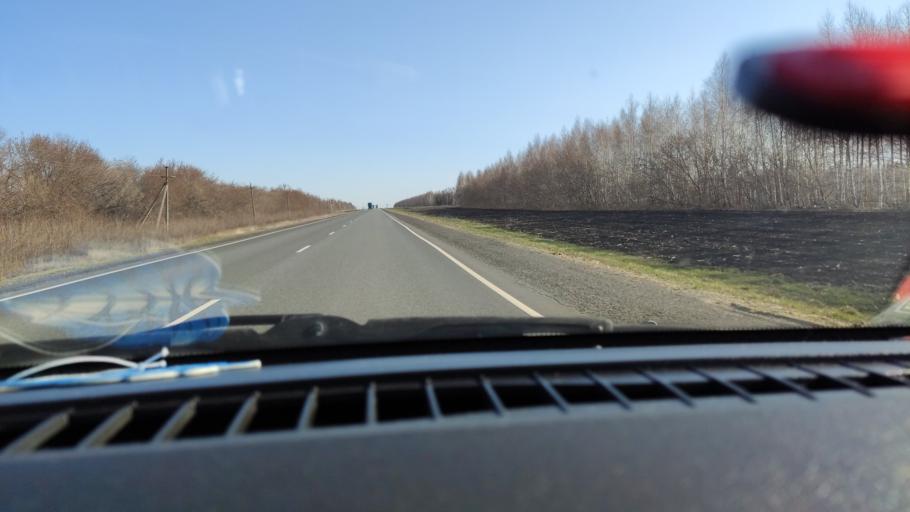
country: RU
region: Samara
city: Syzran'
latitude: 52.9832
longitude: 48.3148
